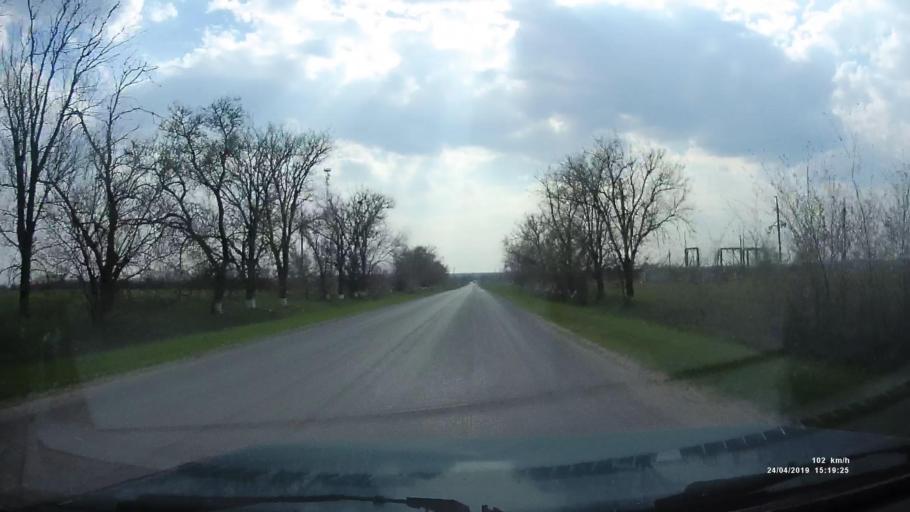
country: RU
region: Rostov
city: Remontnoye
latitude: 46.5402
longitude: 43.1468
